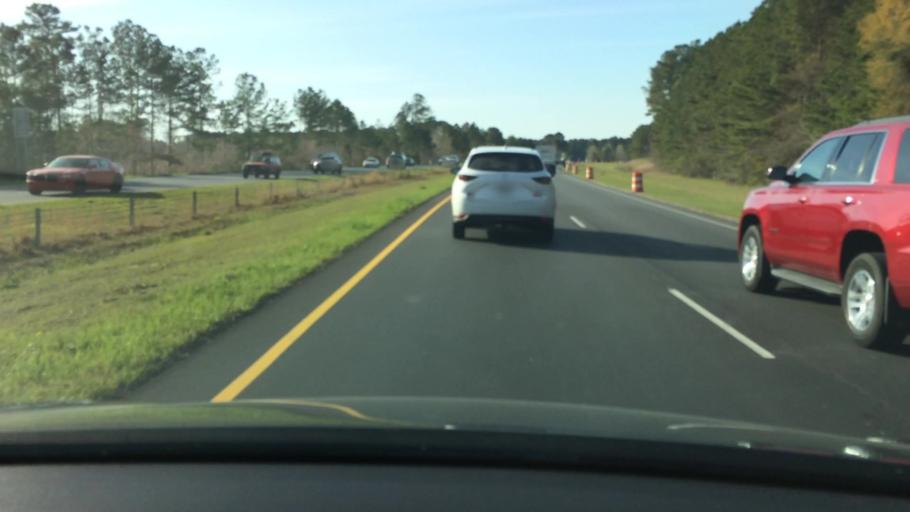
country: US
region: North Carolina
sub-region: Johnston County
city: Pine Level
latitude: 35.4958
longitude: -78.2767
